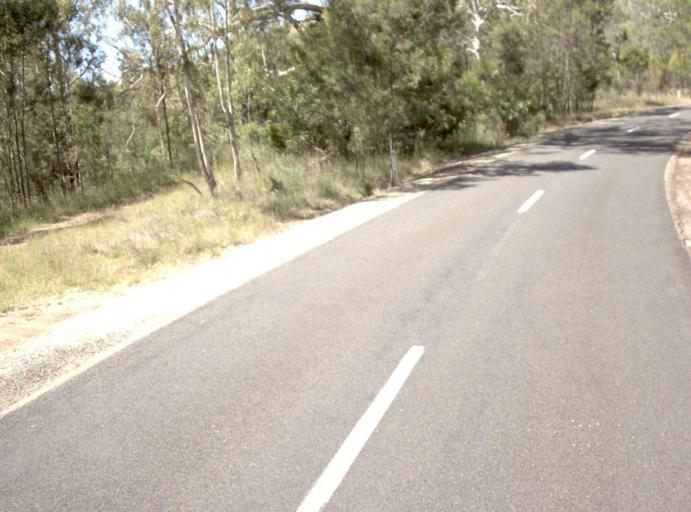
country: AU
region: Victoria
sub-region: East Gippsland
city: Lakes Entrance
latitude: -37.4418
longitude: 148.1930
